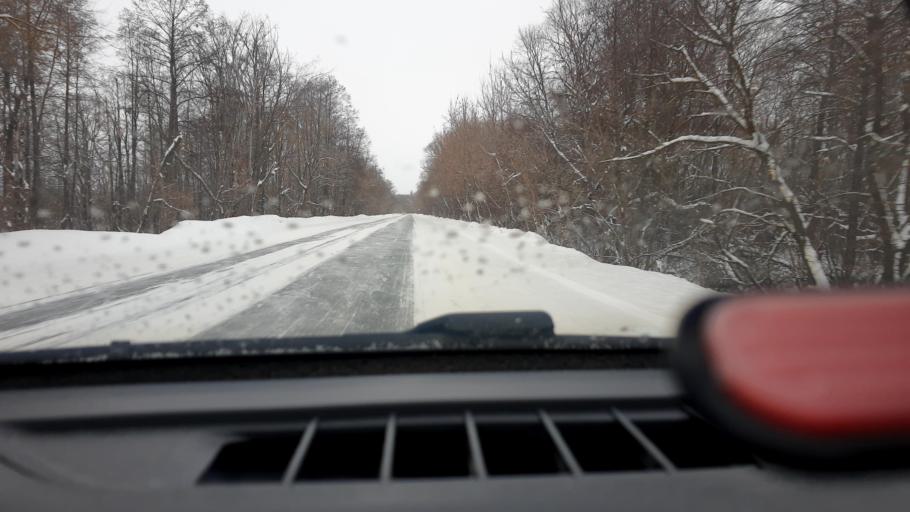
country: RU
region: Nizjnij Novgorod
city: Buturlino
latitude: 55.5834
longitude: 44.9170
